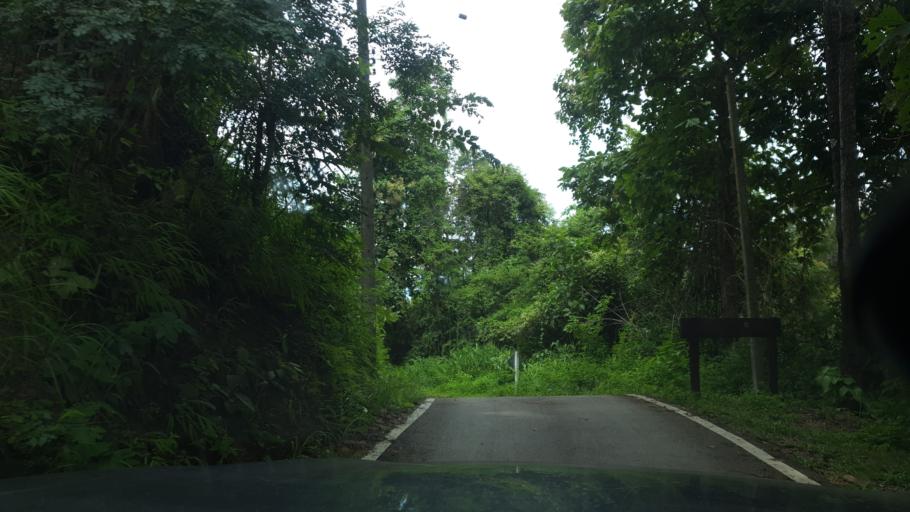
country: TH
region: Lamphun
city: Mae Tha
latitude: 18.5047
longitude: 99.2663
